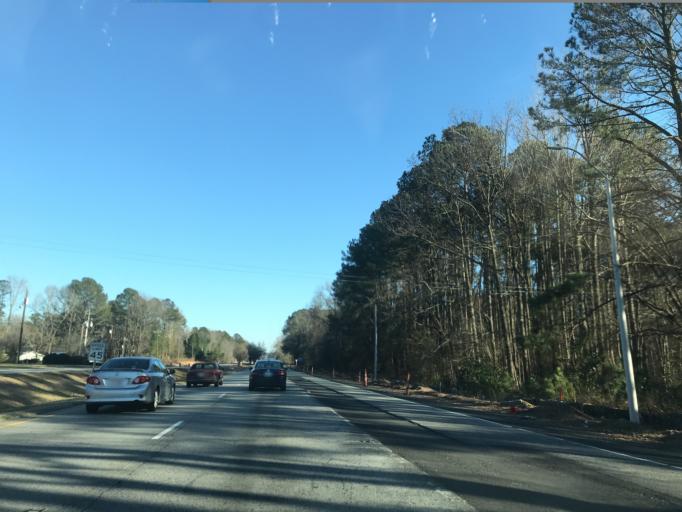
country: US
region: North Carolina
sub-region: Wake County
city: Garner
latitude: 35.7056
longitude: -78.6113
